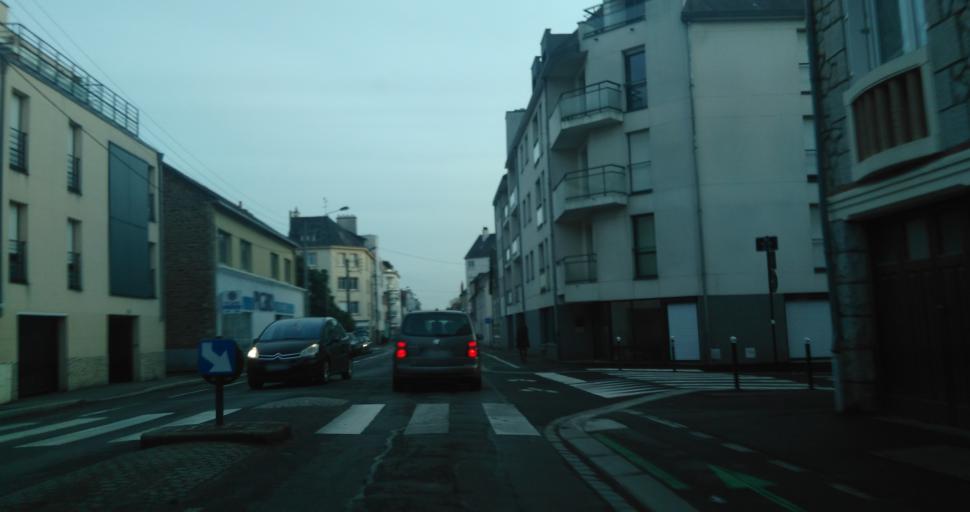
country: FR
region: Brittany
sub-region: Departement d'Ille-et-Vilaine
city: Rennes
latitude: 48.1196
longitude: -1.6610
